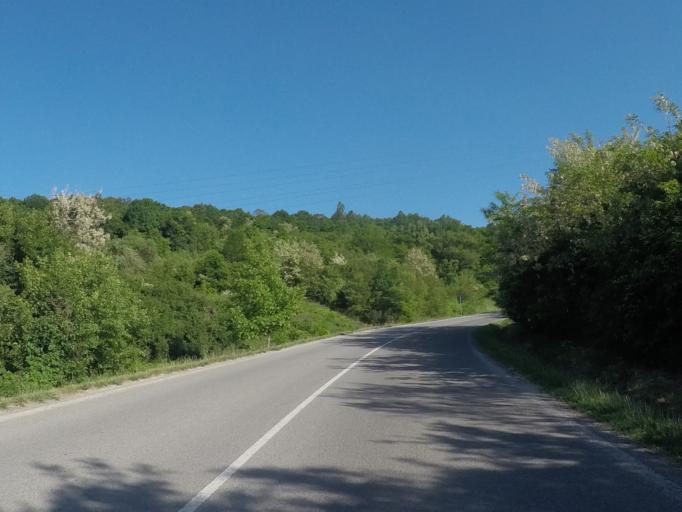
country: SK
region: Kosicky
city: Roznava
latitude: 48.5427
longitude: 20.4075
